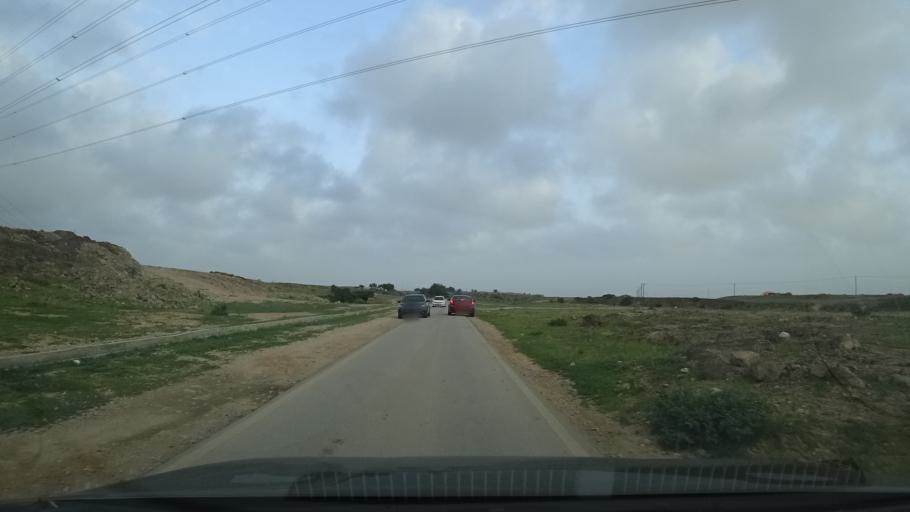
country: OM
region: Zufar
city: Salalah
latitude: 17.1046
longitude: 54.2312
